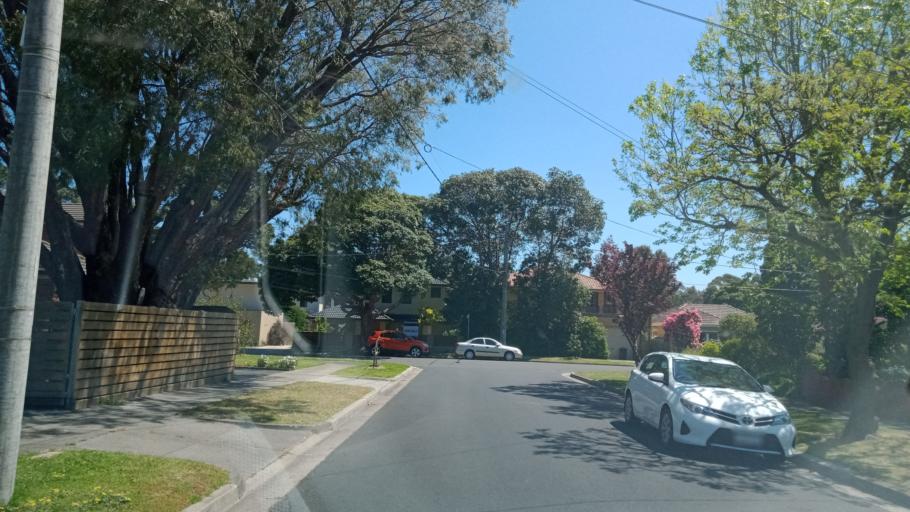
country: AU
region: Victoria
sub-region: Monash
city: Oakleigh South
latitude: -37.9278
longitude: 145.0792
